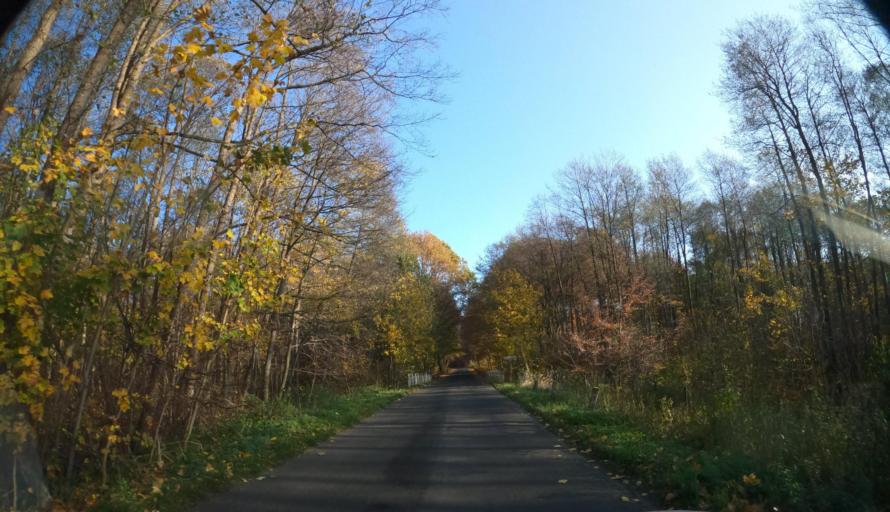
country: PL
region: West Pomeranian Voivodeship
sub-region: Powiat koszalinski
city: Polanow
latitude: 54.2400
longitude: 16.7259
